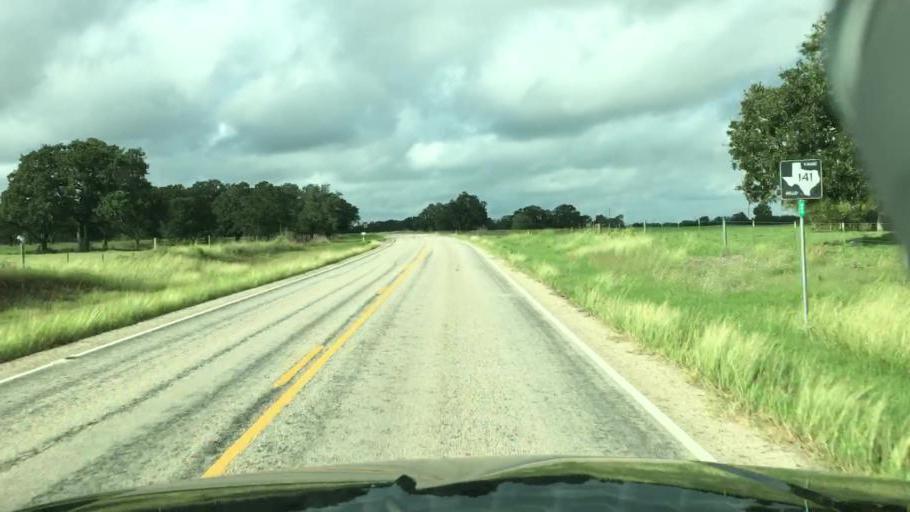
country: US
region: Texas
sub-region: Lee County
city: Giddings
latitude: 30.2602
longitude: -96.8325
